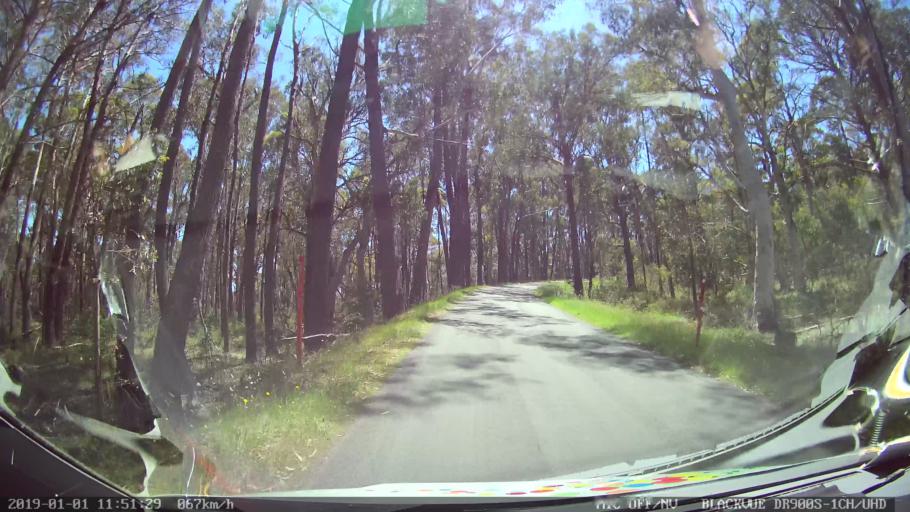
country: AU
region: New South Wales
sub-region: Snowy River
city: Jindabyne
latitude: -35.8848
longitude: 148.4305
